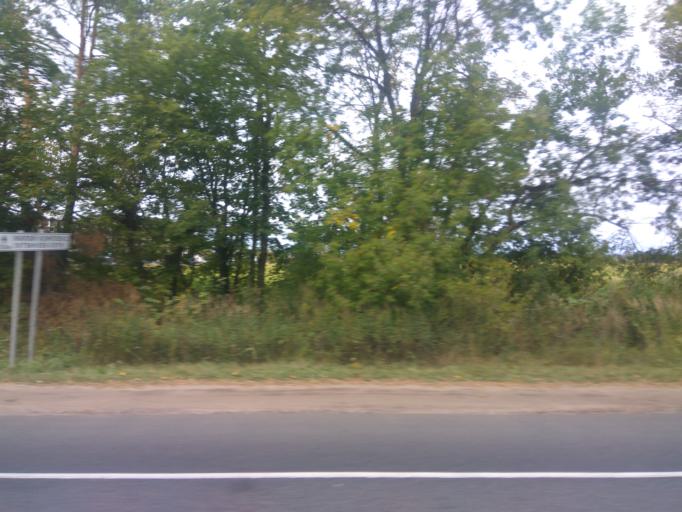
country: RU
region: Moskovskaya
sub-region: Shchelkovskiy Rayon
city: Grebnevo
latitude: 56.0081
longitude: 38.1454
